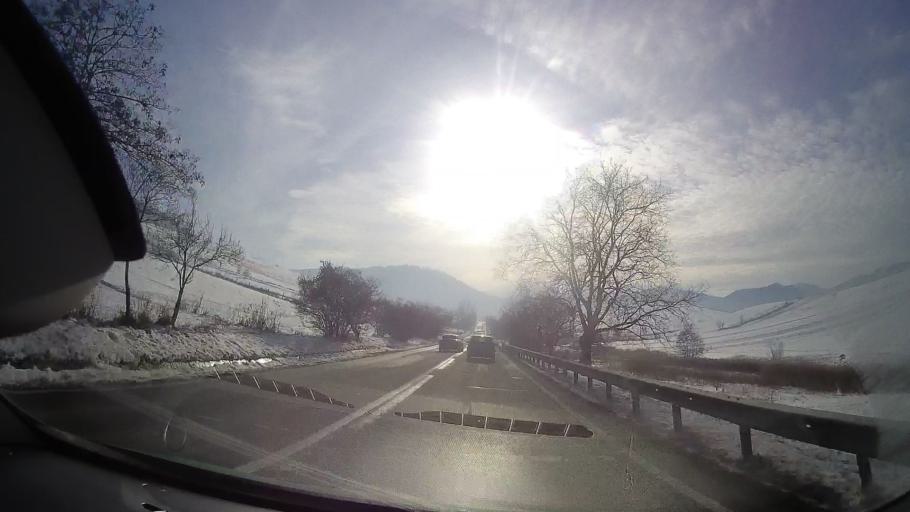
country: RO
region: Neamt
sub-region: Comuna Garcina
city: Garcina
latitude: 46.9879
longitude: 26.3606
